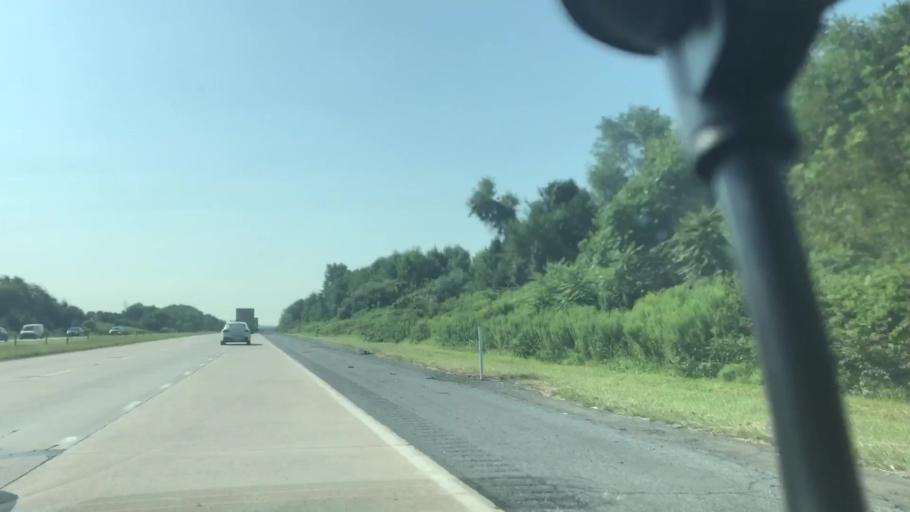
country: US
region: Pennsylvania
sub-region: Montgomery County
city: Limerick
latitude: 40.2130
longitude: -75.5420
